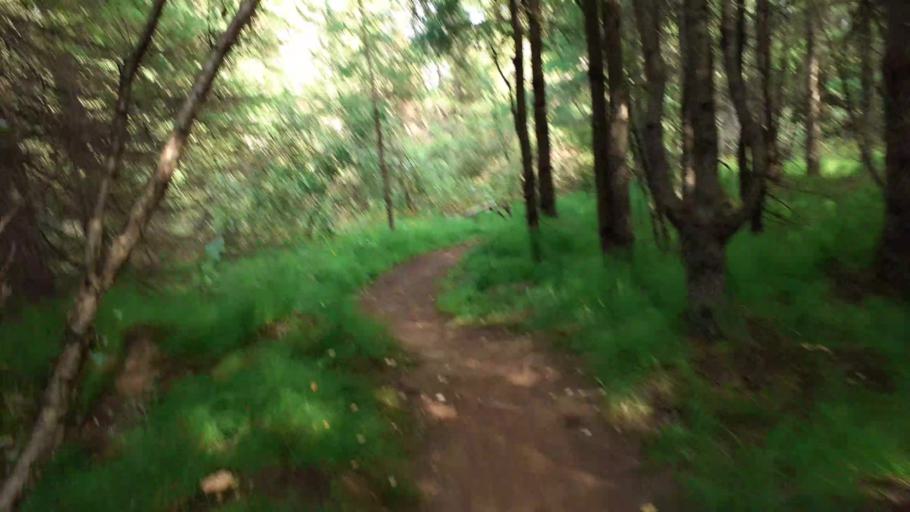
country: IS
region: Northeast
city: Akureyri
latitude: 65.6415
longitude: -18.0844
